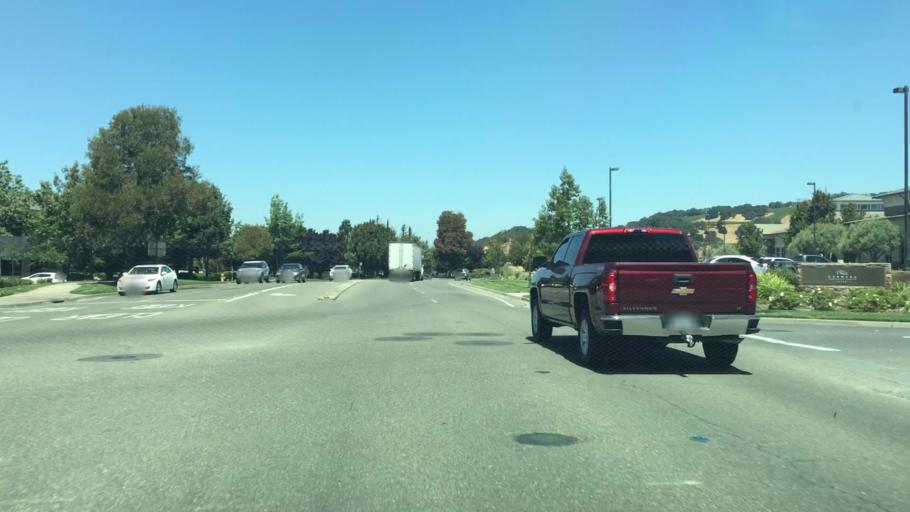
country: US
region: California
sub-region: Napa County
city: American Canyon
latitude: 38.2244
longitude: -122.2627
